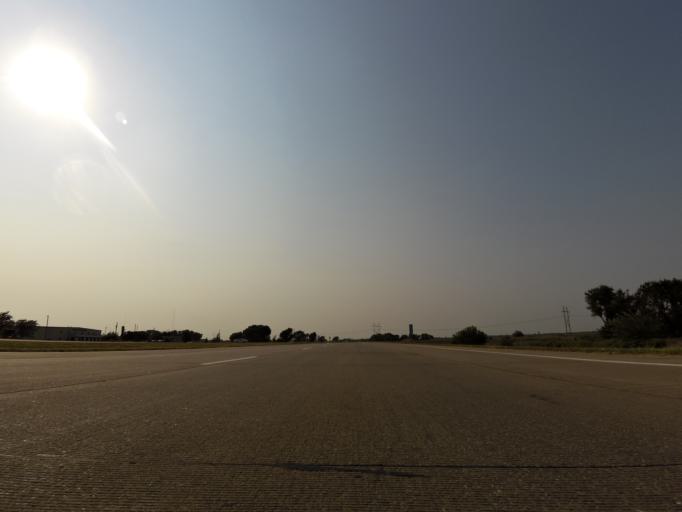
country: US
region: Kansas
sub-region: Sedgwick County
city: Maize
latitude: 37.7946
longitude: -97.4797
